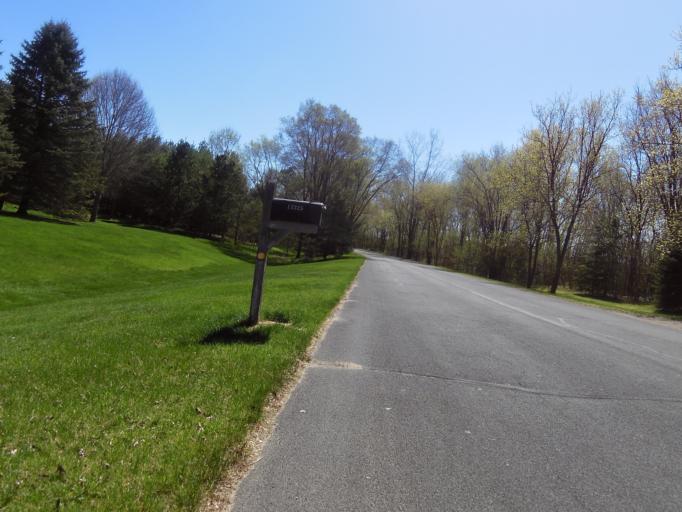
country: US
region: Minnesota
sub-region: Washington County
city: Lake Elmo
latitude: 44.9541
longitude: -92.8335
